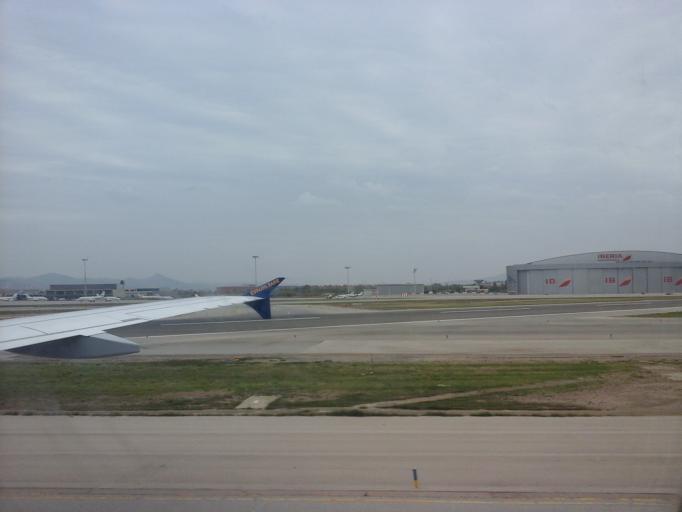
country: ES
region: Catalonia
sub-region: Provincia de Barcelona
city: El Prat de Llobregat
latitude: 41.3048
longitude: 2.0938
